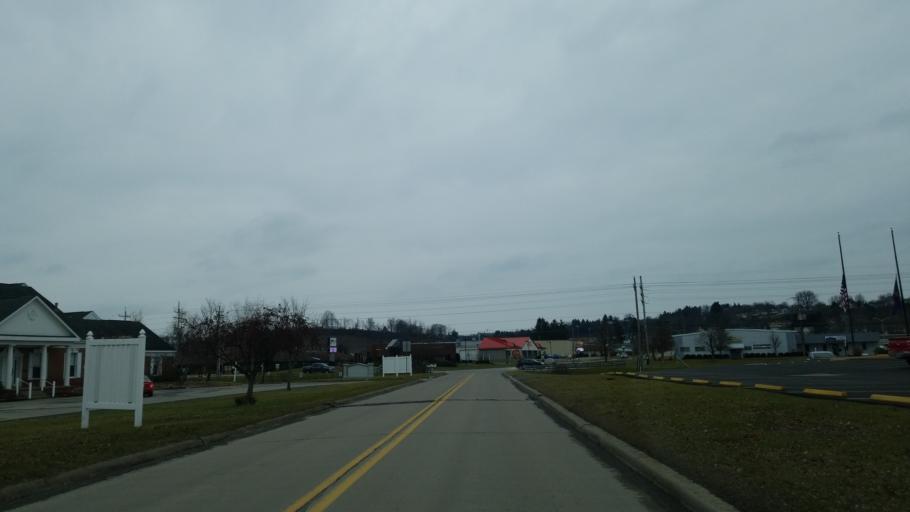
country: US
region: Pennsylvania
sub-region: Clearfield County
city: DuBois
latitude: 41.1216
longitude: -78.7491
